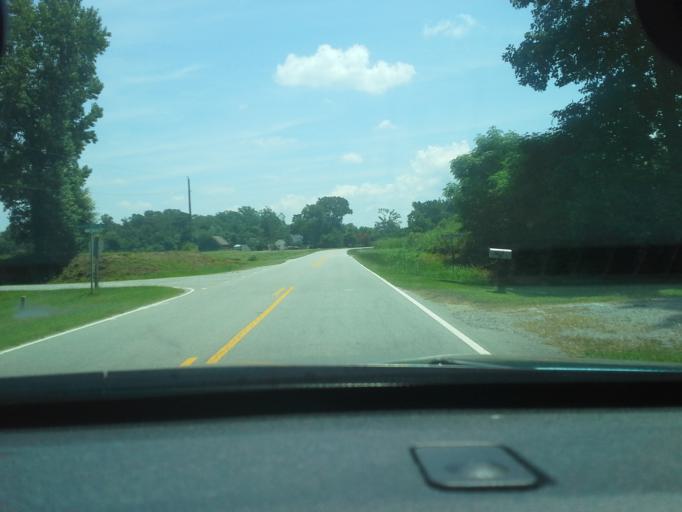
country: US
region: North Carolina
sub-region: Chowan County
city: Edenton
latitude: 35.9296
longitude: -76.6072
